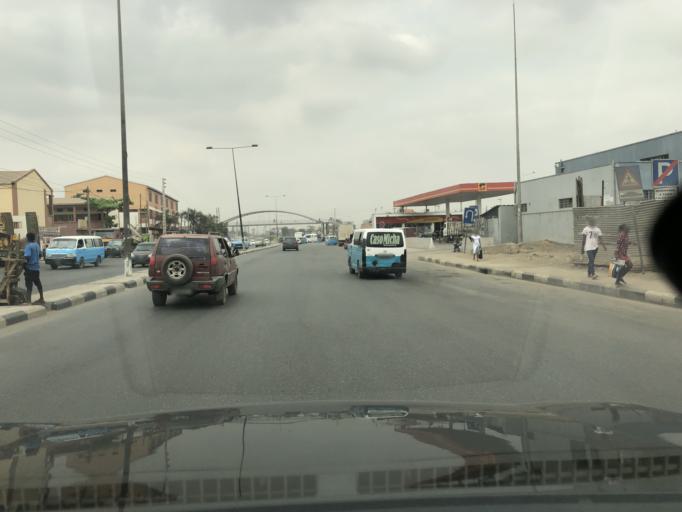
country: AO
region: Luanda
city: Luanda
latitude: -8.8375
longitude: 13.2838
